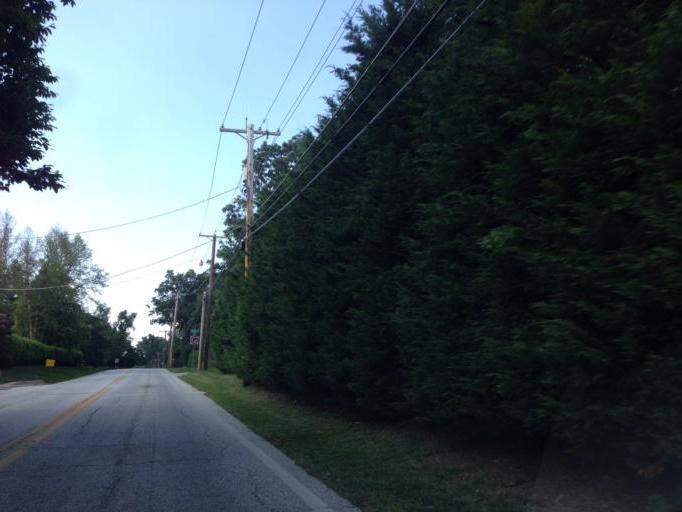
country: US
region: Maryland
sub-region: Baltimore County
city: Towson
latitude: 39.3902
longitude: -76.5901
